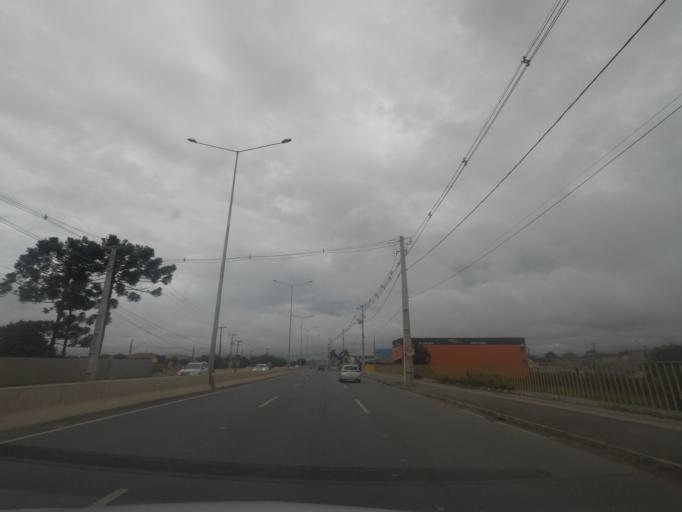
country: BR
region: Parana
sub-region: Pinhais
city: Pinhais
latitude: -25.4412
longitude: -49.1525
